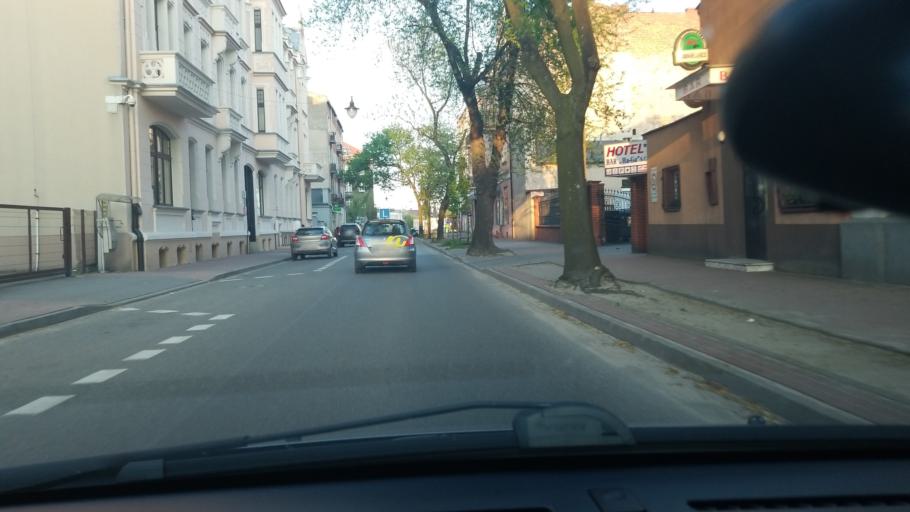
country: PL
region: Silesian Voivodeship
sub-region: Czestochowa
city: Czestochowa
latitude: 50.8104
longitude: 19.1247
